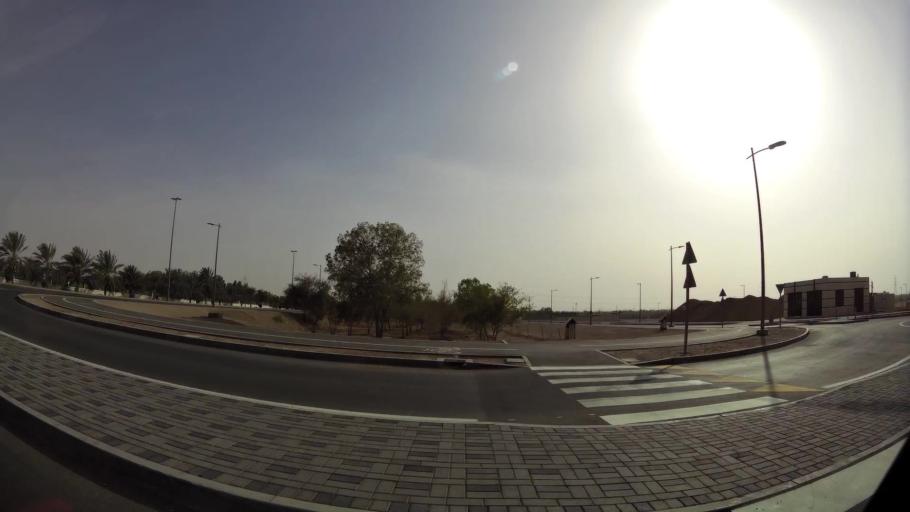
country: AE
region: Abu Dhabi
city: Al Ain
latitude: 24.1078
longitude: 55.7275
